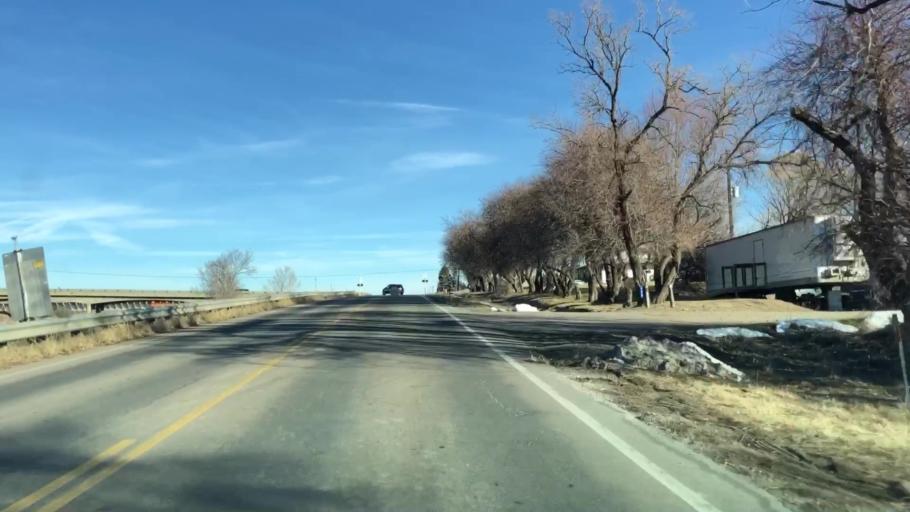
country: US
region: Colorado
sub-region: Larimer County
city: Loveland
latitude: 40.3985
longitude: -104.9928
